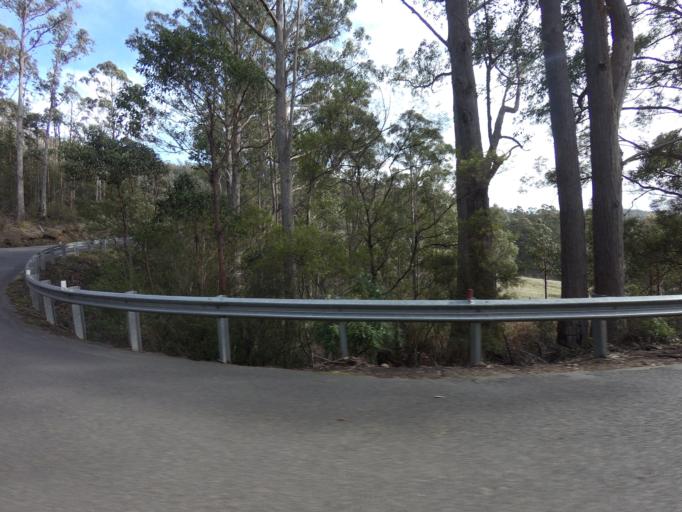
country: AU
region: Tasmania
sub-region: Kingborough
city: Margate
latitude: -43.0070
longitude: 147.1691
